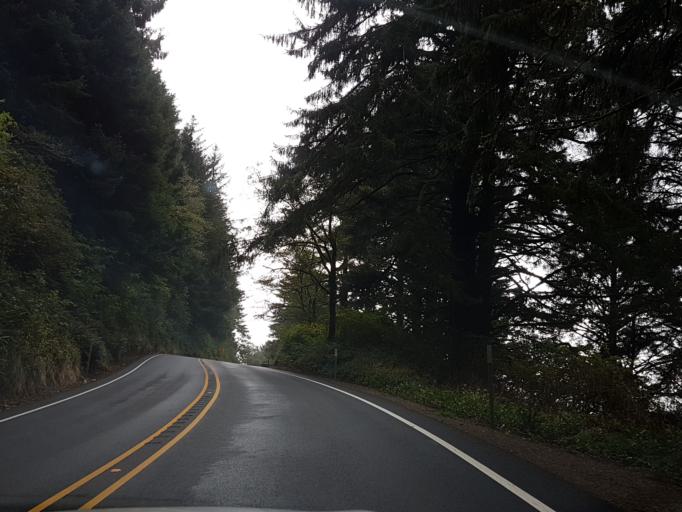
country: US
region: Oregon
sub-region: Lane County
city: Florence
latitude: 44.1168
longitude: -124.1202
